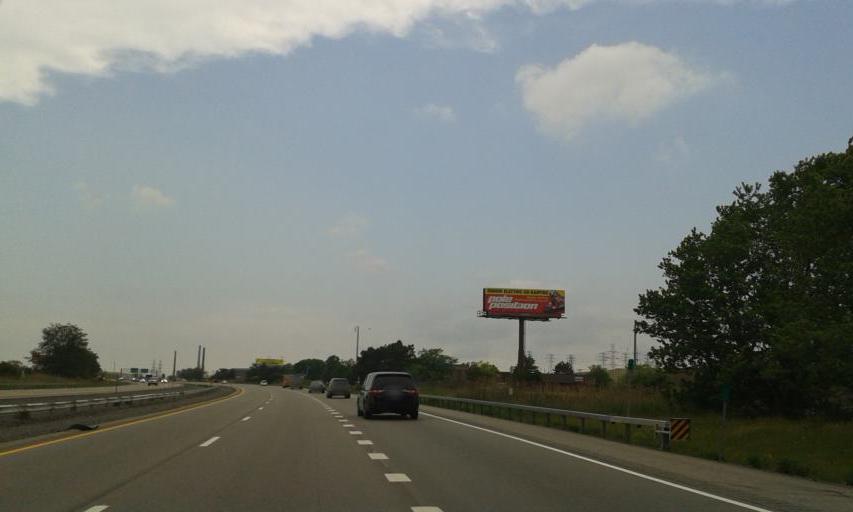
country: US
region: New York
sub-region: Erie County
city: Tonawanda
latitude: 42.9922
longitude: -78.9029
